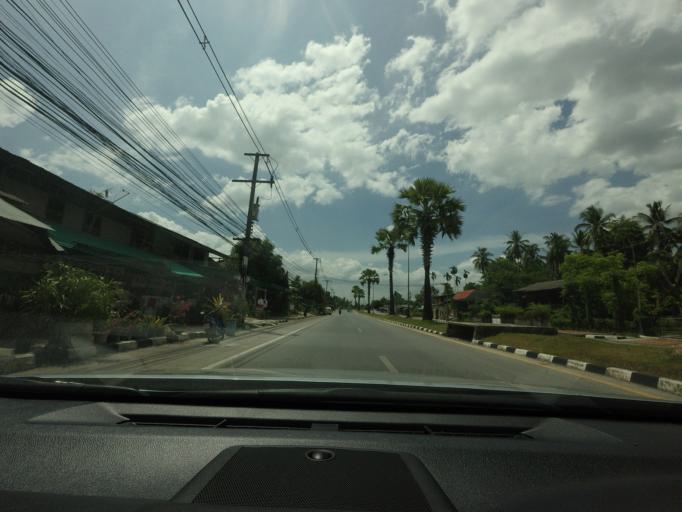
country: TH
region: Yala
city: Raman
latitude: 6.4550
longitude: 101.3463
